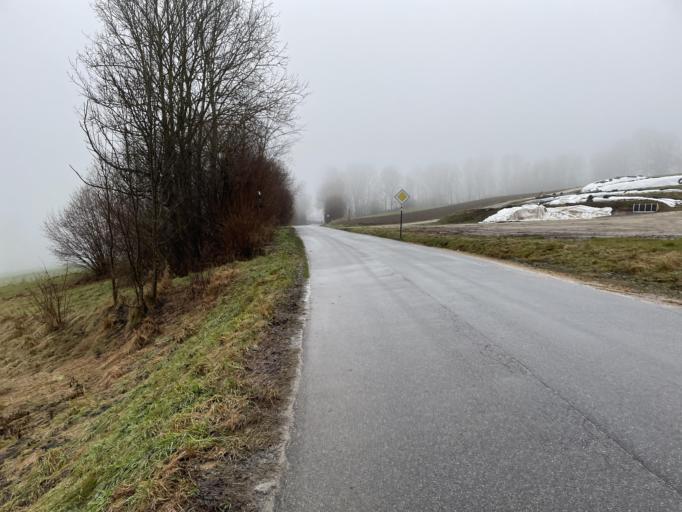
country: DE
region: Bavaria
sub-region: Lower Bavaria
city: Ruhmannsfelden
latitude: 48.9946
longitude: 13.0109
